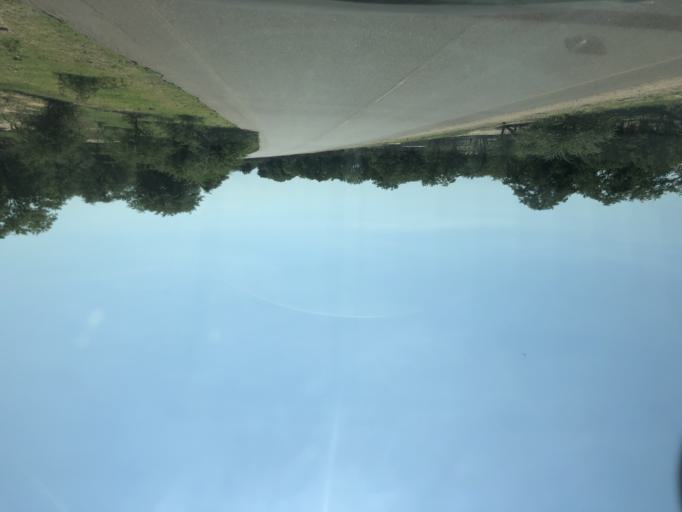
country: AO
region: Cunene
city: Ondjiva
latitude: -16.7100
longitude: 15.3088
